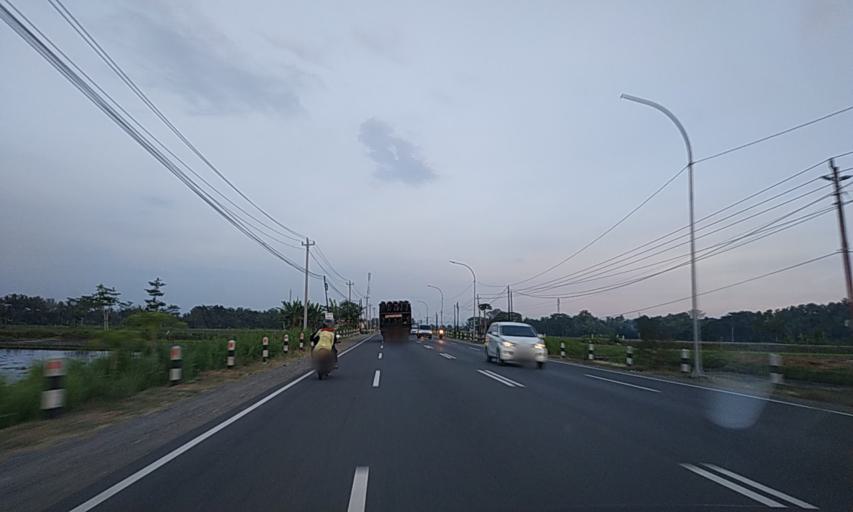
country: ID
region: Daerah Istimewa Yogyakarta
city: Srandakan
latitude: -7.8733
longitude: 110.2002
